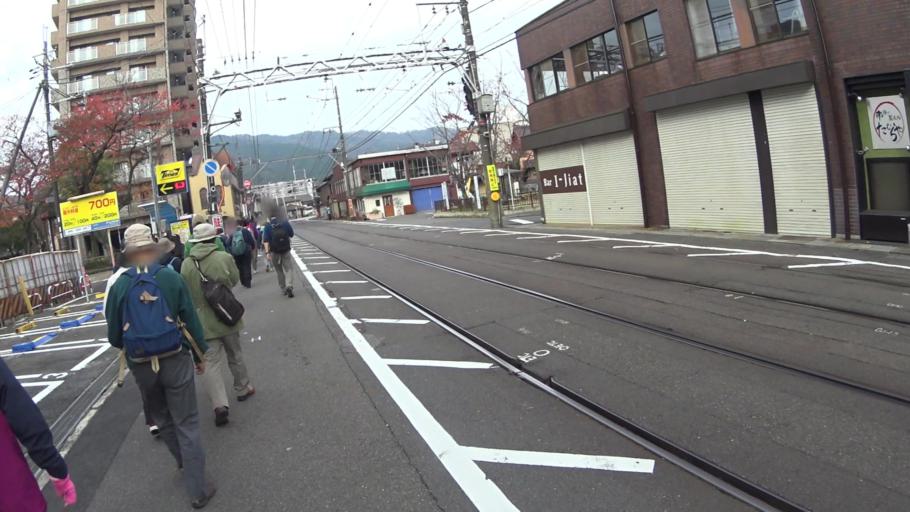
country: JP
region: Shiga Prefecture
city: Otsu-shi
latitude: 35.0119
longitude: 135.8610
